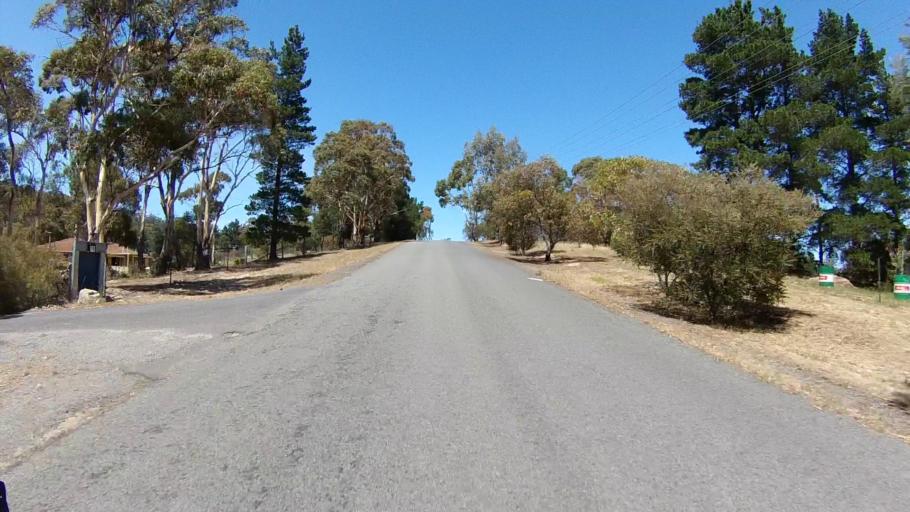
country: AU
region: Tasmania
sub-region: Clarence
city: Cambridge
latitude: -42.8464
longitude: 147.4239
